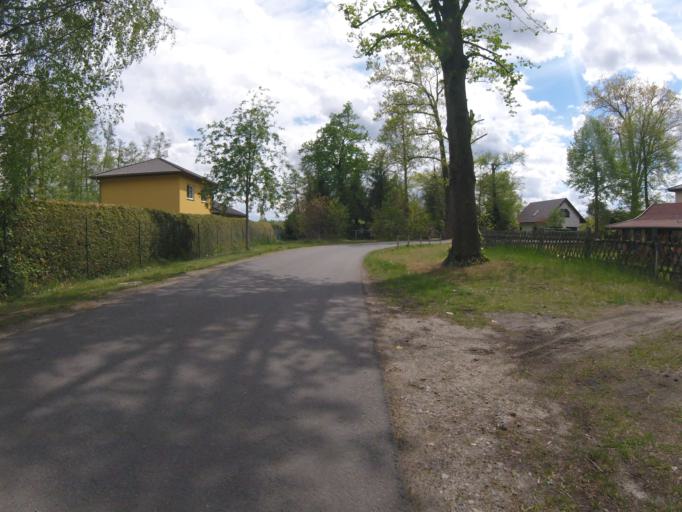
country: DE
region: Brandenburg
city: Schwerin
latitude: 52.1578
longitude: 13.6329
